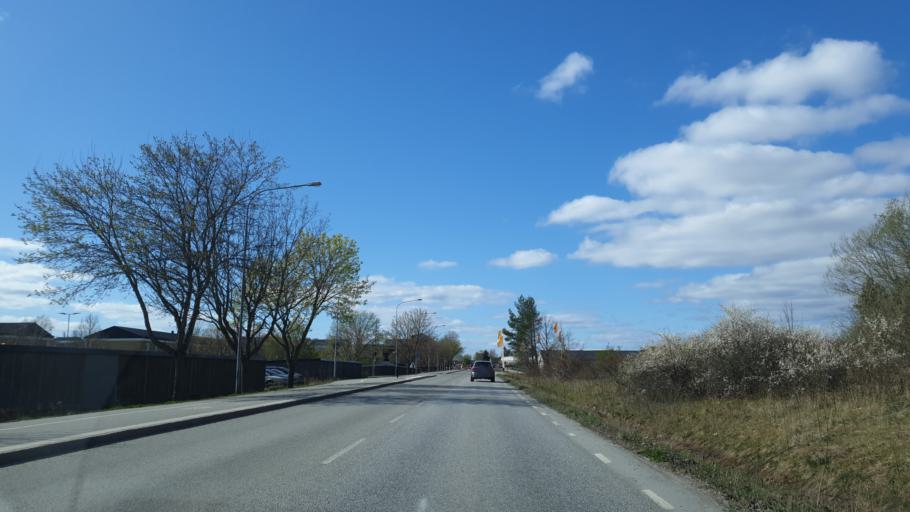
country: SE
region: Uppsala
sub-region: Uppsala Kommun
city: Gamla Uppsala
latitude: 59.8896
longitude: 17.6558
